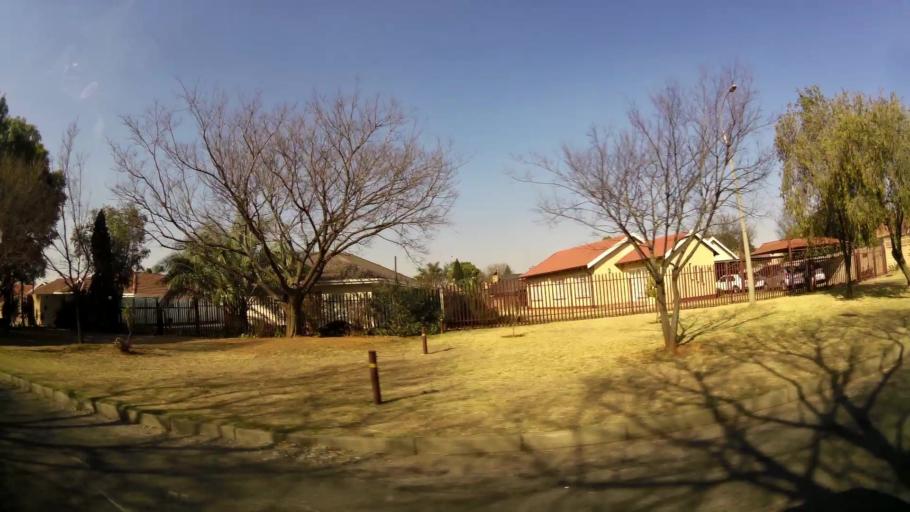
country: ZA
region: Gauteng
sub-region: West Rand District Municipality
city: Randfontein
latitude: -26.1823
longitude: 27.6857
